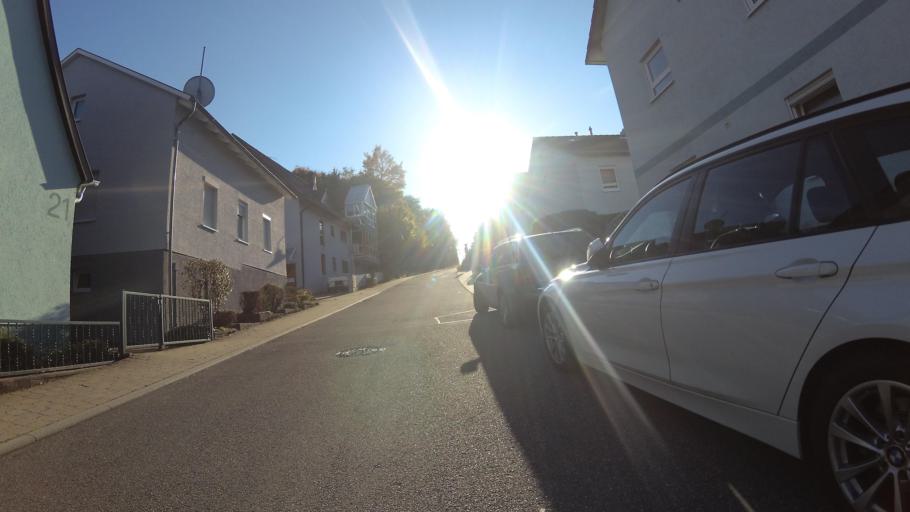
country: DE
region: Baden-Wuerttemberg
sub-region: Regierungsbezirk Stuttgart
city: Oedheim
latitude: 49.2375
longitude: 9.2514
